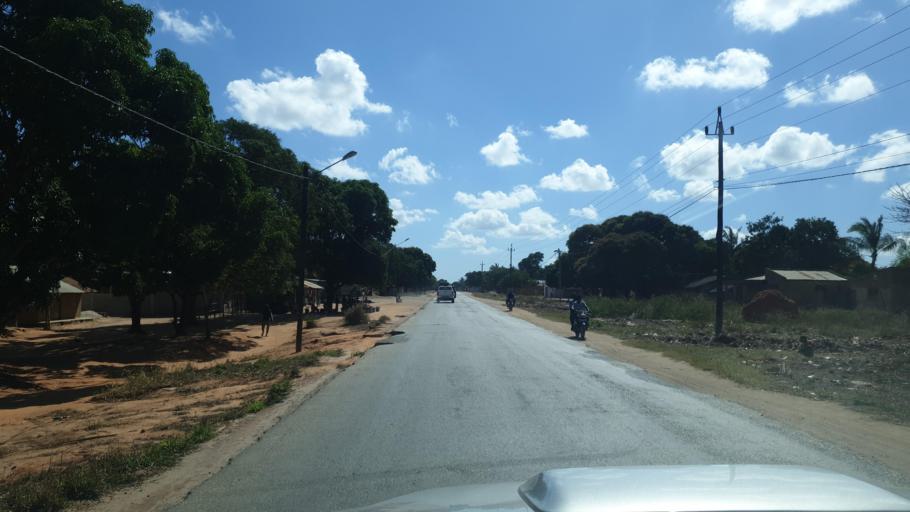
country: MZ
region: Nampula
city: Nacala
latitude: -14.5147
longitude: 40.6968
